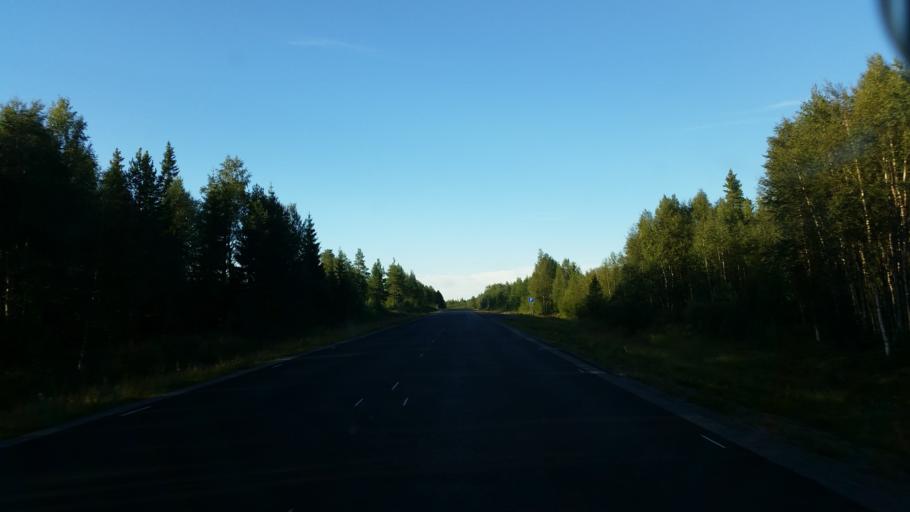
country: SE
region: Vaesterbotten
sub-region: Dorotea Kommun
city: Dorotea
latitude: 64.3293
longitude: 16.6308
